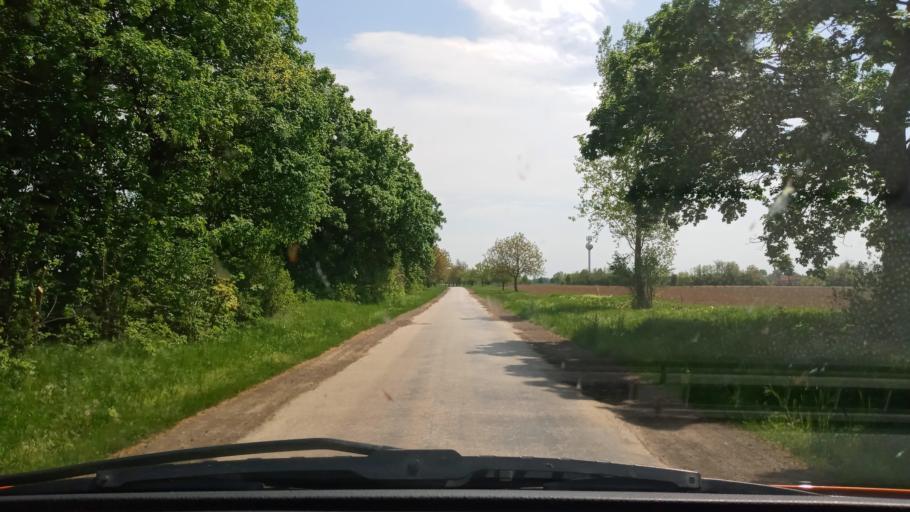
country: HU
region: Baranya
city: Villany
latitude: 45.8247
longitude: 18.5040
